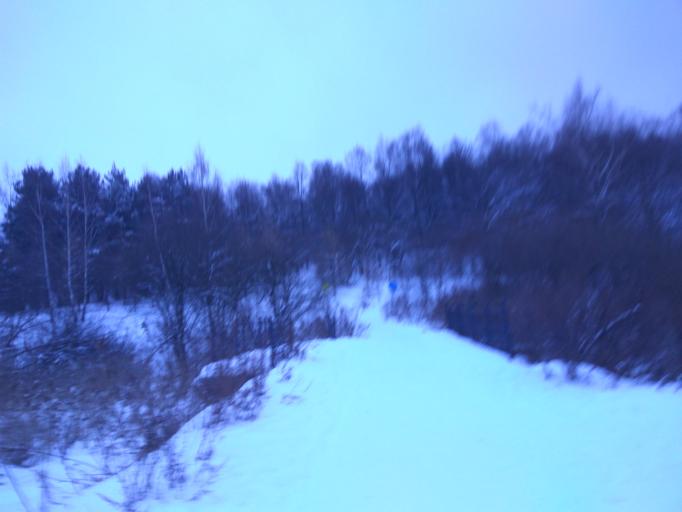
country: RU
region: Moscow
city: Orekhovo-Borisovo
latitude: 55.5985
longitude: 37.7077
